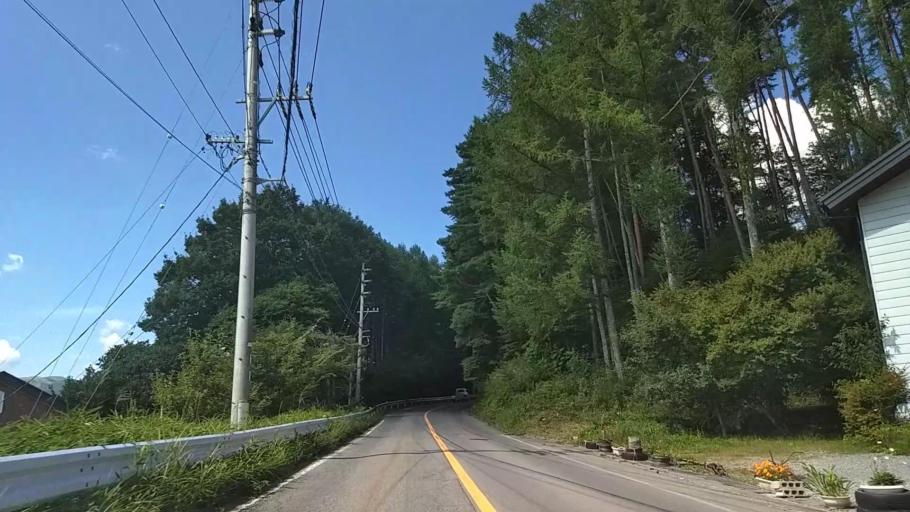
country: JP
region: Nagano
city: Chino
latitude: 36.0334
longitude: 138.2307
